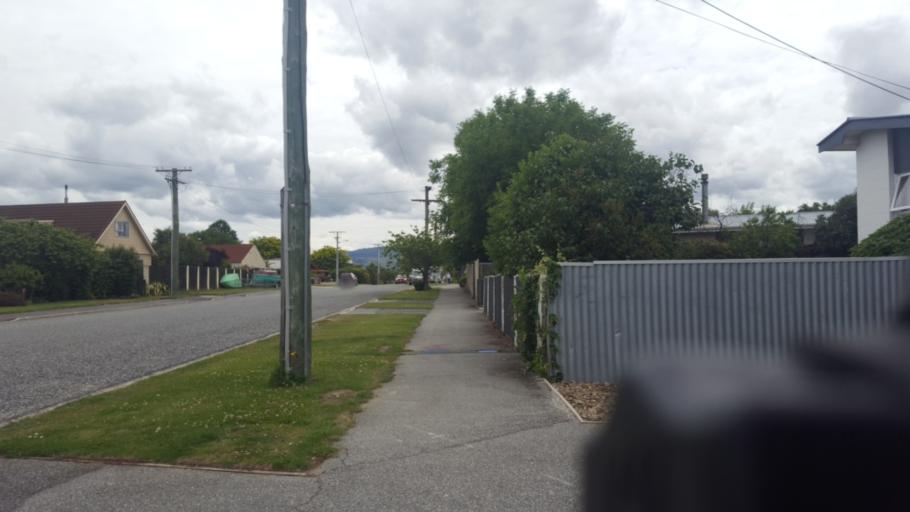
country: NZ
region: Otago
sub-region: Queenstown-Lakes District
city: Wanaka
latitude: -45.2541
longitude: 169.3872
